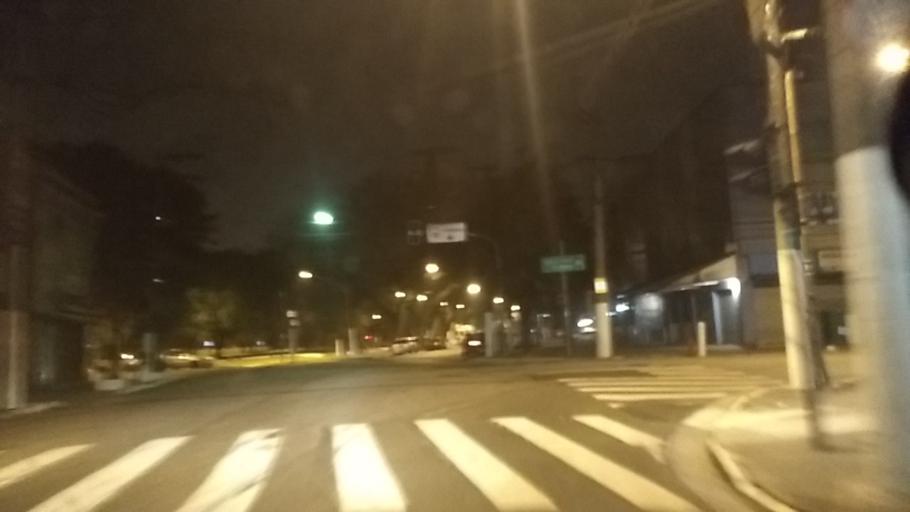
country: BR
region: Sao Paulo
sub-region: Sao Paulo
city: Sao Paulo
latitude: -23.5310
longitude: -46.6020
